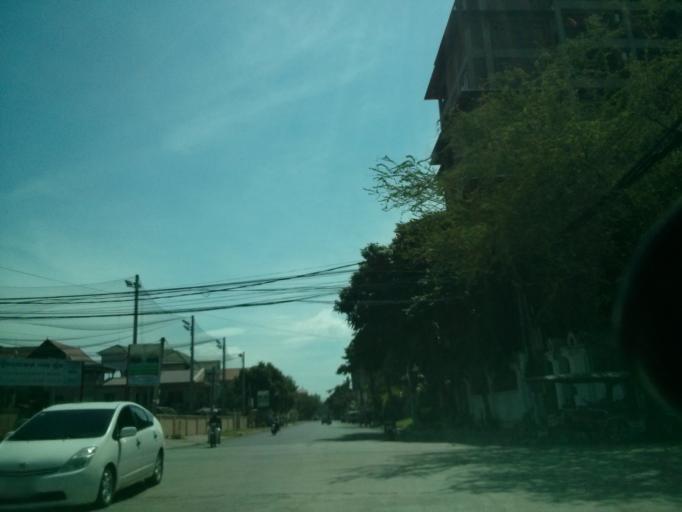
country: KH
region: Phnom Penh
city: Phnom Penh
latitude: 11.5826
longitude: 104.8919
